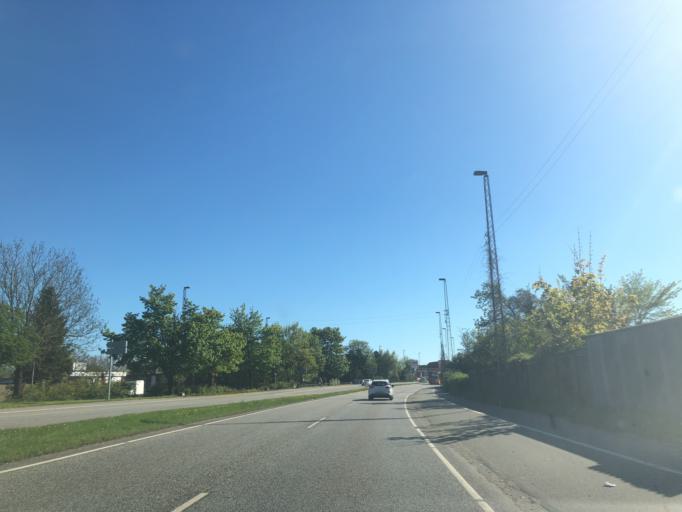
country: DK
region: Zealand
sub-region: Koge Kommune
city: Koge
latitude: 55.4490
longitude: 12.1744
